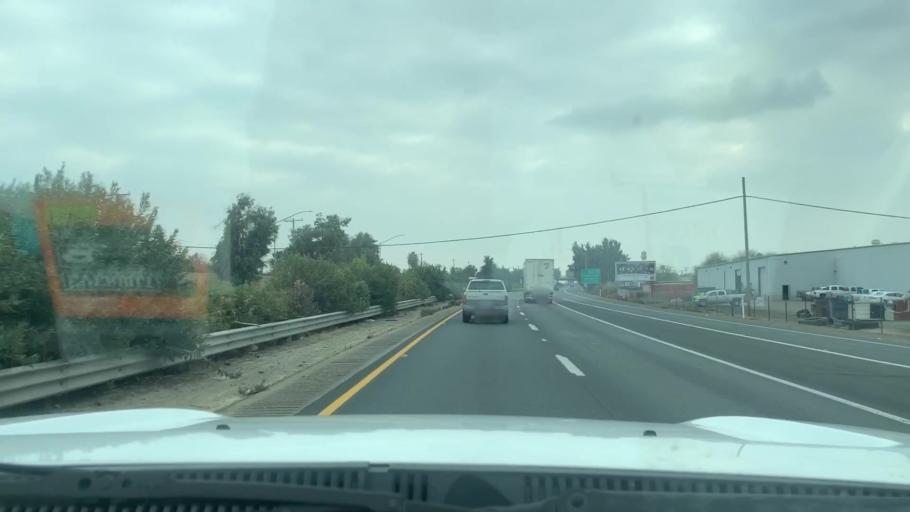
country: US
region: California
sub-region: Tulare County
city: Tipton
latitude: 36.0637
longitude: -119.3133
